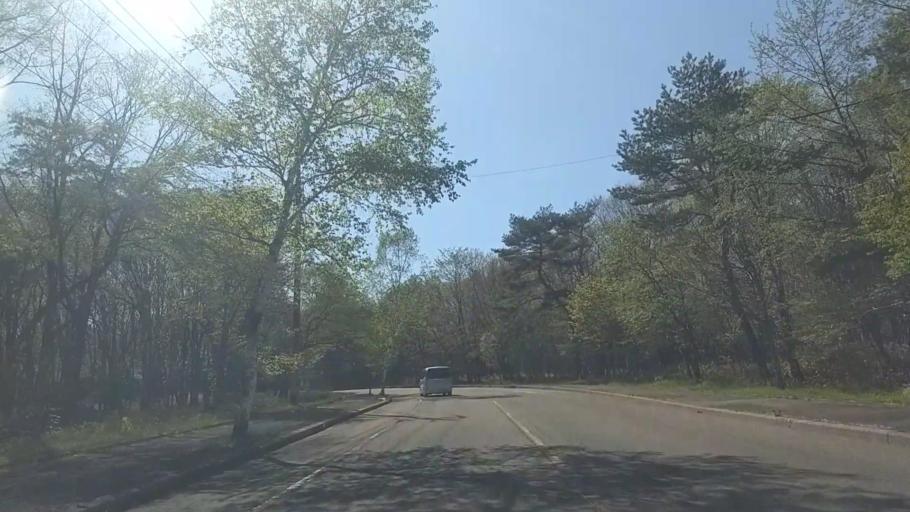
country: JP
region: Yamanashi
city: Nirasaki
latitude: 35.9414
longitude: 138.4369
